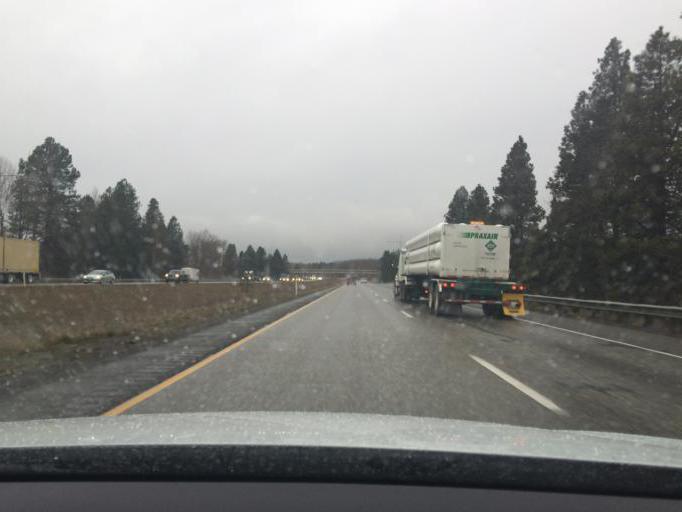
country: US
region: Washington
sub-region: Kittitas County
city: Cle Elum
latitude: 47.1809
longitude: -120.8980
